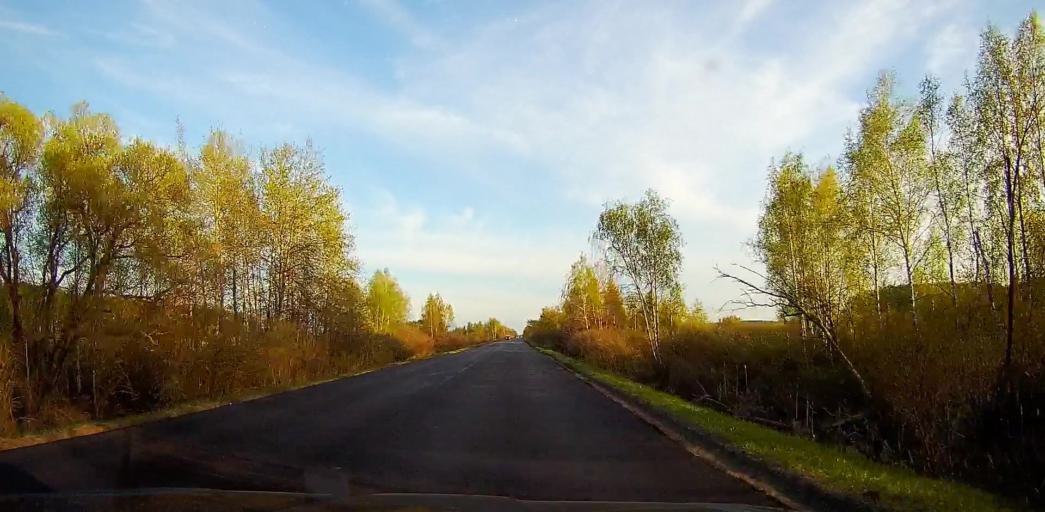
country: RU
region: Moskovskaya
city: Bronnitsy
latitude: 55.2836
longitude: 38.2169
